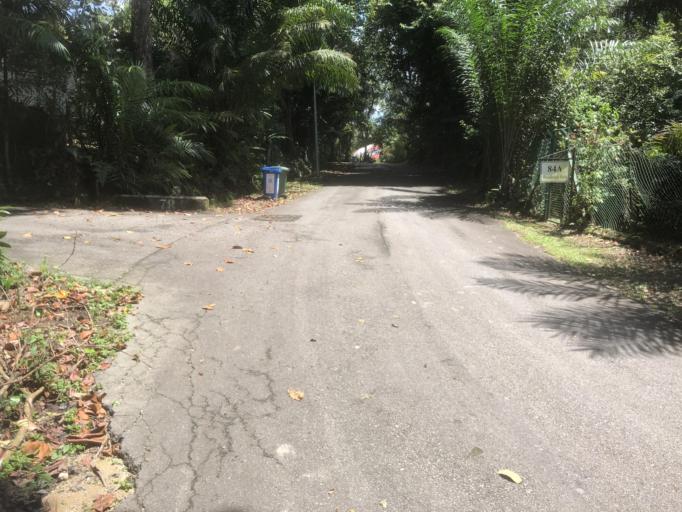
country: SG
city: Singapore
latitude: 1.3419
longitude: 103.8657
